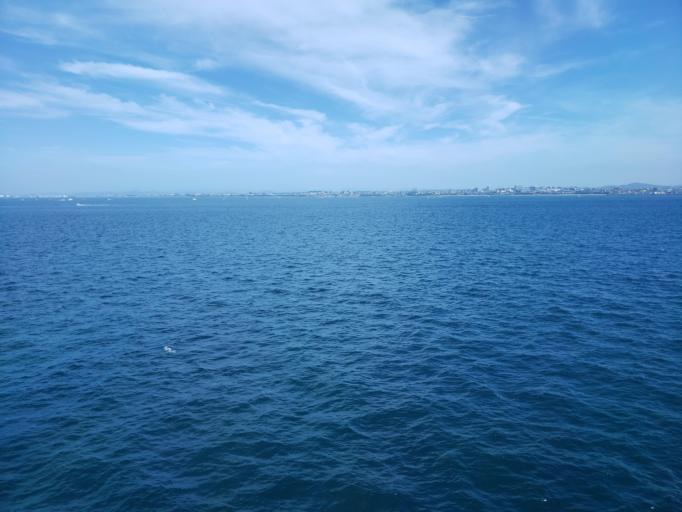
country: JP
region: Hyogo
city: Akashi
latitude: 34.6209
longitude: 134.9568
